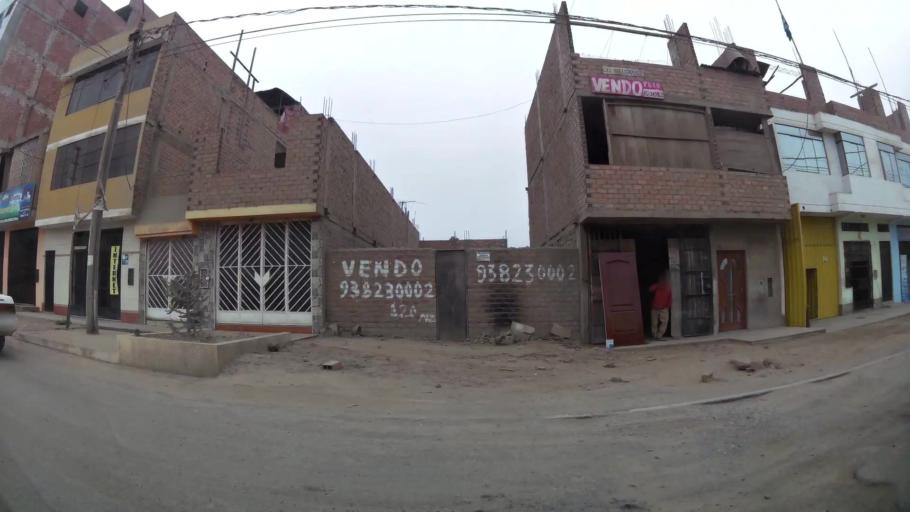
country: PE
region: Lima
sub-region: Lima
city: Urb. Santo Domingo
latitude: -11.8748
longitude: -77.0309
